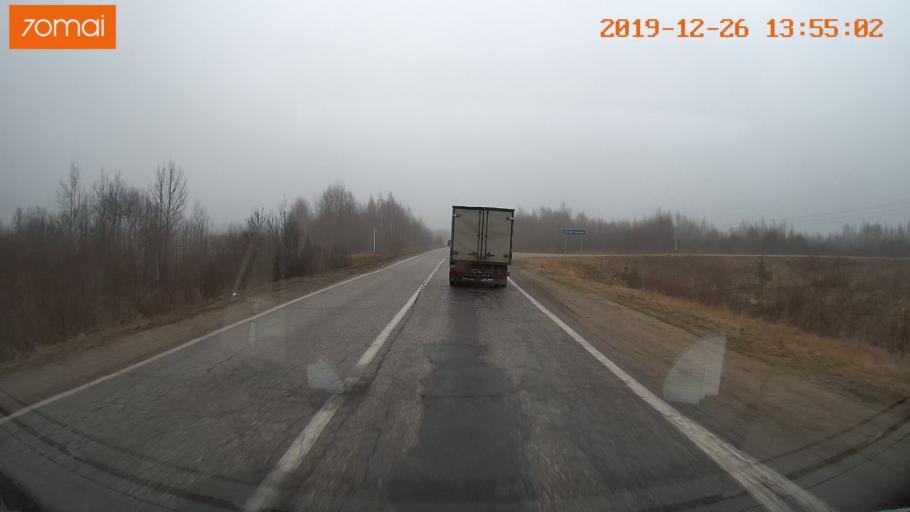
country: RU
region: Jaroslavl
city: Poshekhon'ye
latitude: 58.6075
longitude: 38.6425
